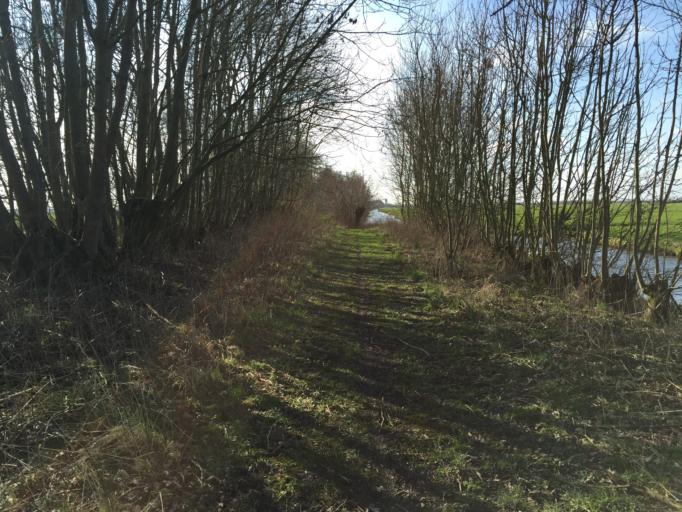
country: NL
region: Utrecht
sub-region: Gemeente Lopik
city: Lopik
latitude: 51.9921
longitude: 4.9556
